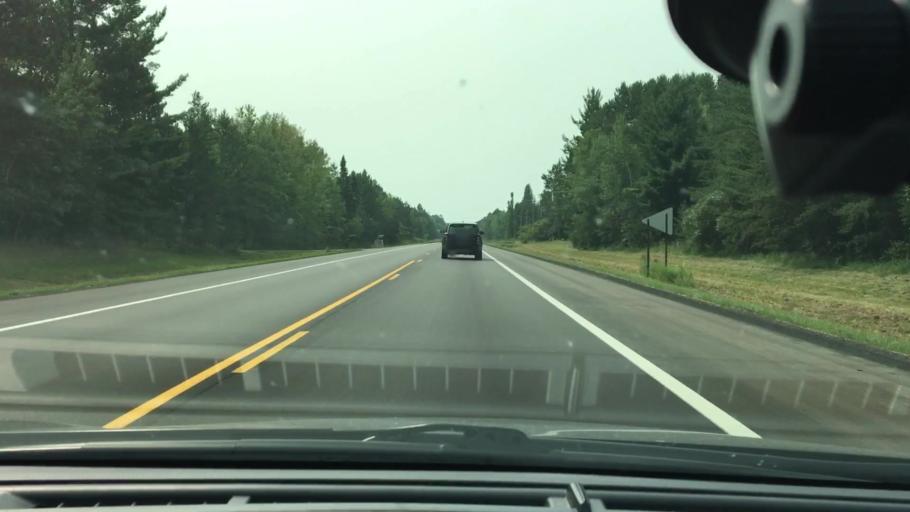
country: US
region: Minnesota
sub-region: Crow Wing County
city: Brainerd
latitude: 46.4487
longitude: -94.1720
